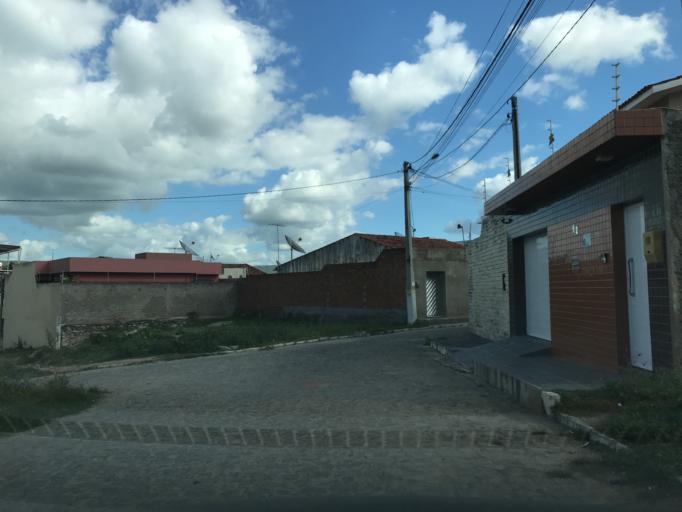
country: BR
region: Pernambuco
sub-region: Bezerros
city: Bezerros
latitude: -8.2323
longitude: -35.7557
